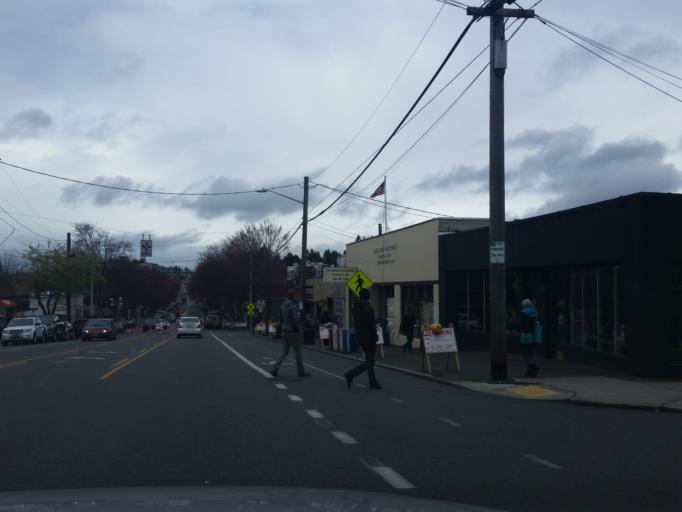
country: US
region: Washington
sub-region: King County
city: Shoreline
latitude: 47.6891
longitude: -122.3553
